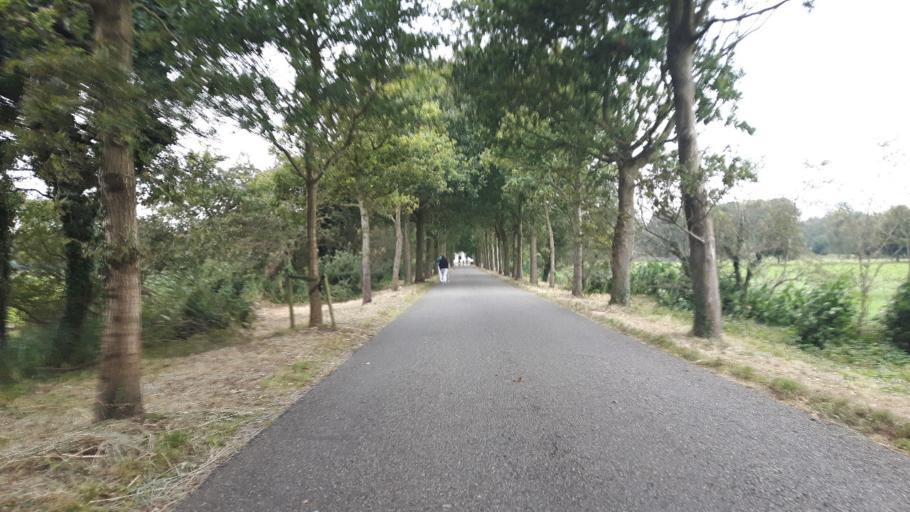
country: NL
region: North Holland
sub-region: Gemeente Bloemendaal
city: Bennebroek
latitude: 52.3265
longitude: 4.5765
